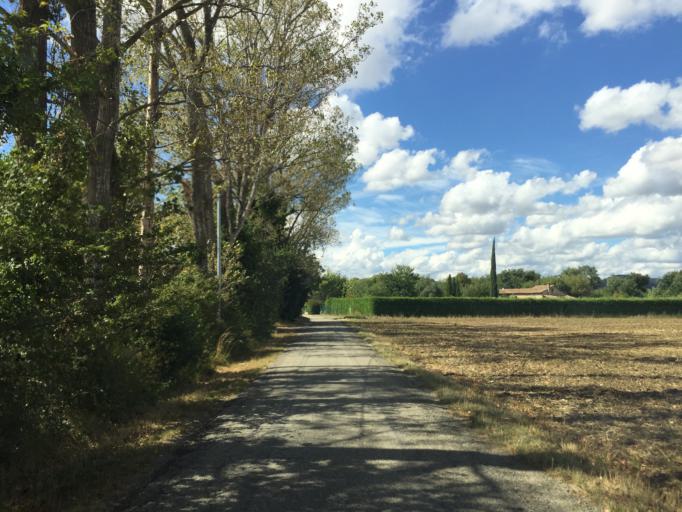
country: FR
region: Provence-Alpes-Cote d'Azur
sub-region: Departement du Vaucluse
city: Caderousse
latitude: 44.1325
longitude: 4.7400
